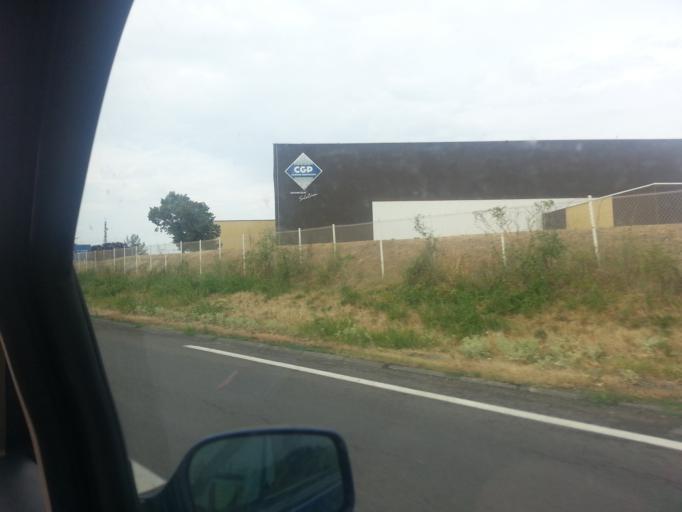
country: FR
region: Auvergne
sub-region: Departement du Puy-de-Dome
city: Cebazat
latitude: 45.8397
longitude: 3.1146
